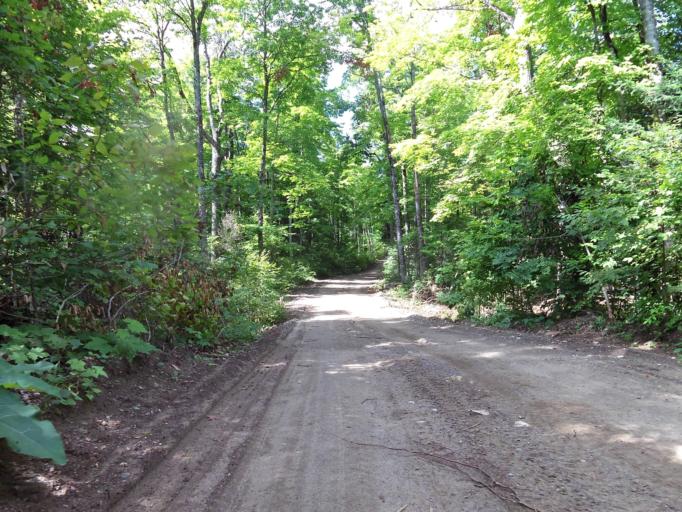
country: CA
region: Ontario
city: Renfrew
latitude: 45.1280
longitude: -76.7252
